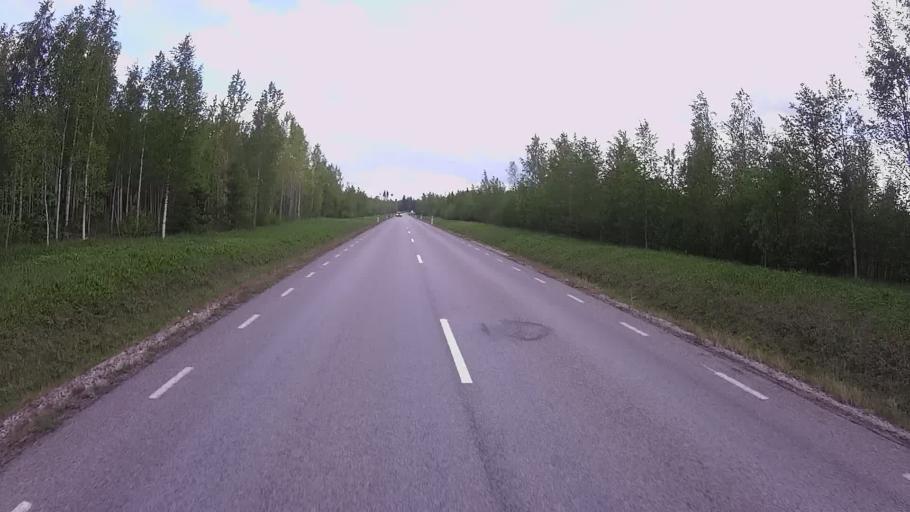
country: EE
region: Jogevamaa
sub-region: Mustvee linn
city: Mustvee
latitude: 59.0847
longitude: 26.9892
